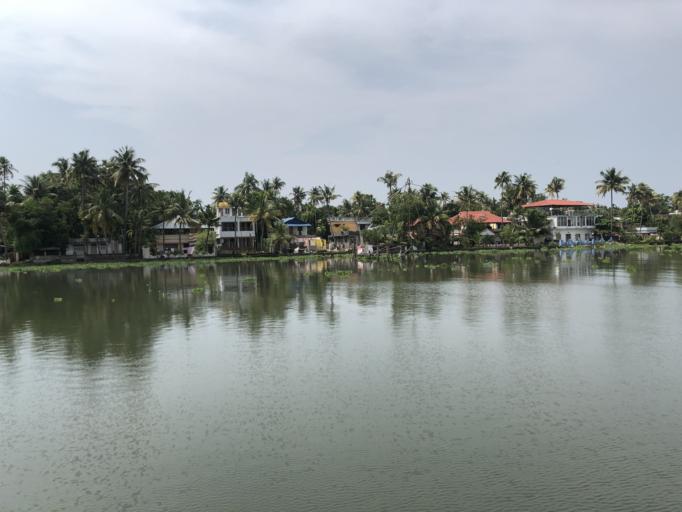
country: IN
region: Kerala
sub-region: Ernakulam
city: Cochin
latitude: 9.9939
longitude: 76.2666
